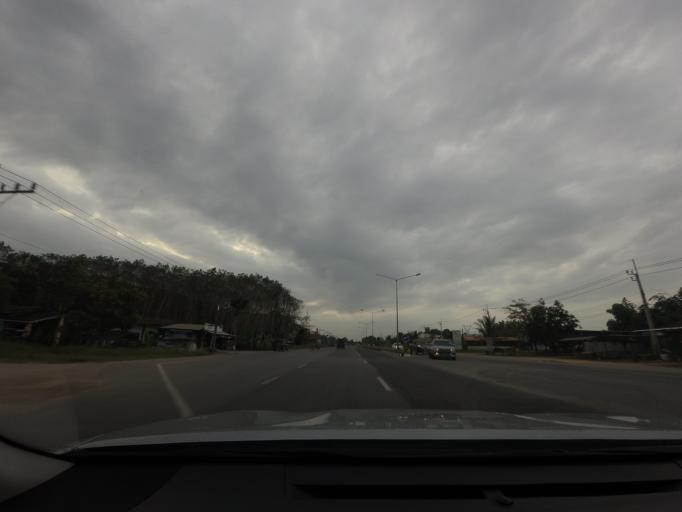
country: TH
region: Surat Thani
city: Phunphin
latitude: 9.0426
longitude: 99.1160
